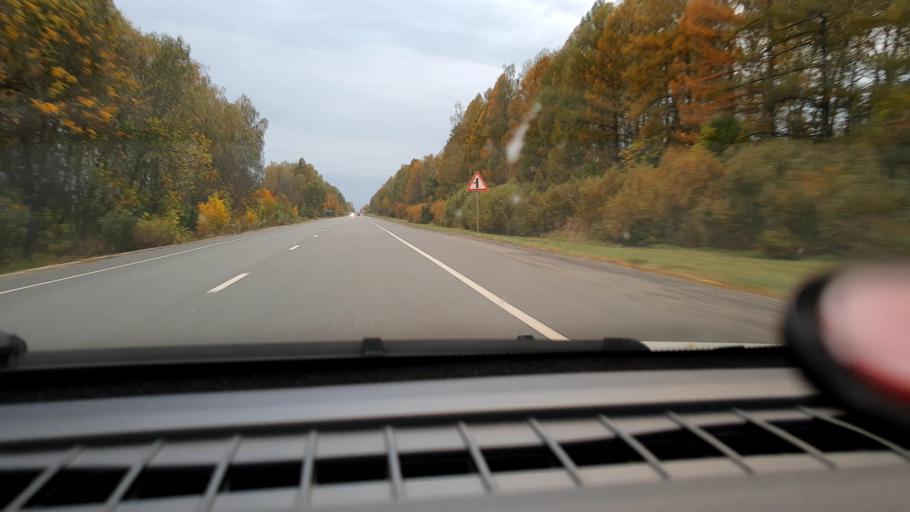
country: RU
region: Vladimir
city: Kameshkovo
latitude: 56.1971
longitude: 40.8661
